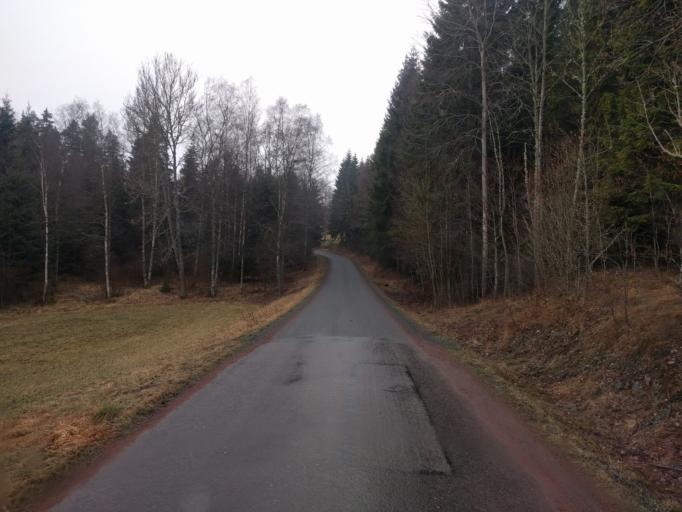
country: SE
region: Joenkoeping
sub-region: Jonkopings Kommun
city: Graenna
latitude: 57.9467
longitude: 14.4600
